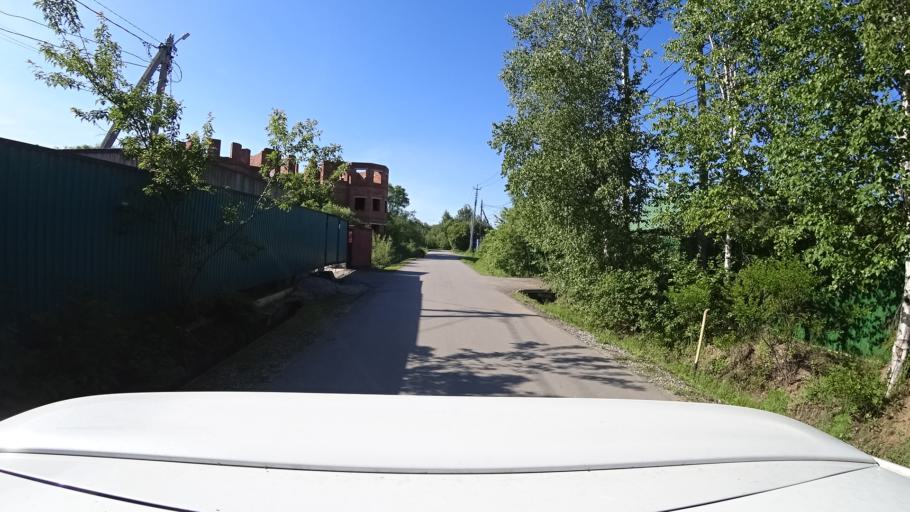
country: RU
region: Khabarovsk Krai
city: Topolevo
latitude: 48.5434
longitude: 135.1789
